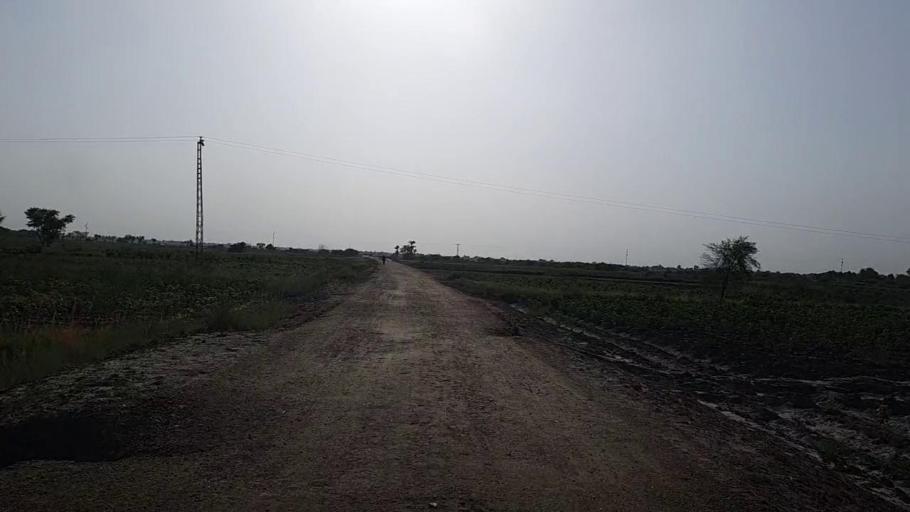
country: PK
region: Sindh
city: Pad Idan
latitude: 26.8531
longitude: 68.3034
